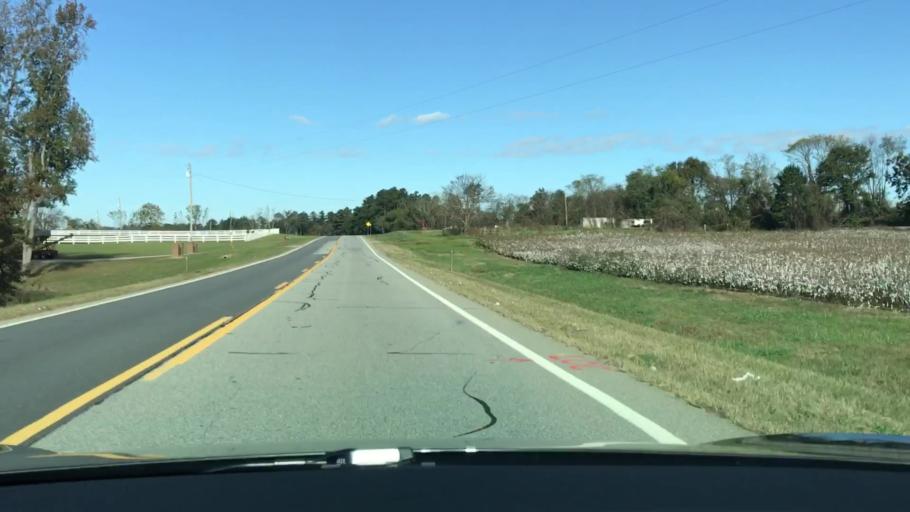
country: US
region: Georgia
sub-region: Warren County
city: Warrenton
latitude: 33.3693
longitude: -82.6007
